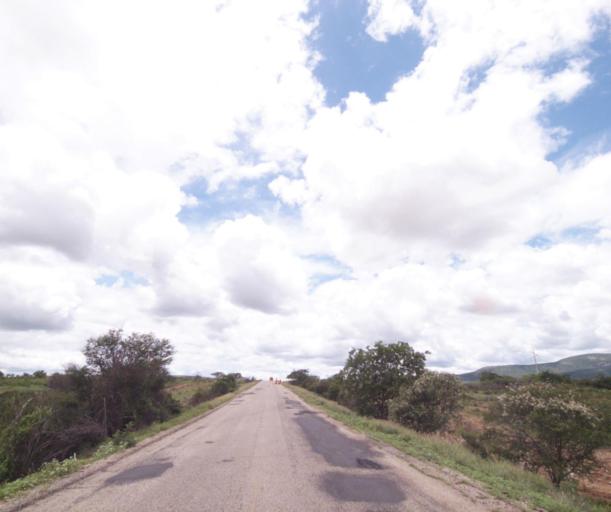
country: BR
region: Bahia
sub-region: Brumado
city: Brumado
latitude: -14.1575
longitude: -41.5219
